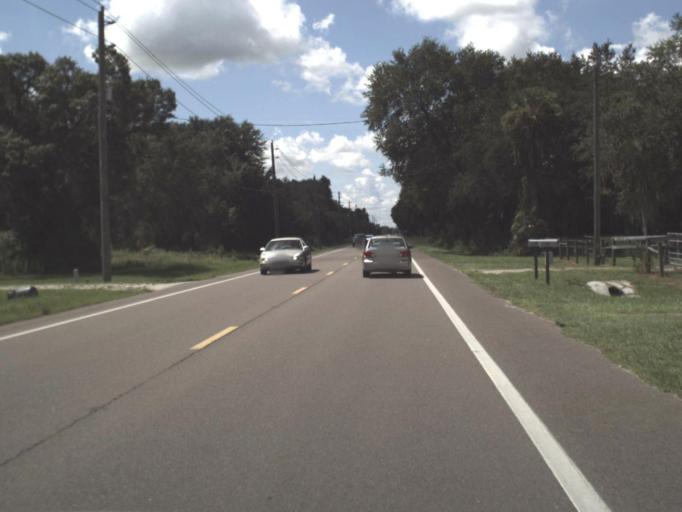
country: US
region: Florida
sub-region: DeSoto County
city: Southeast Arcadia
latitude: 27.1825
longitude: -81.8715
